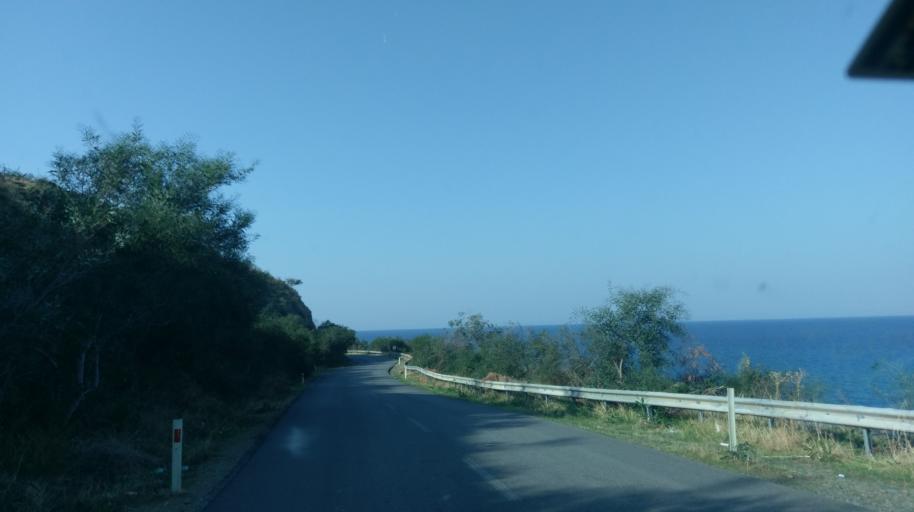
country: CY
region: Lefkosia
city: Lefka
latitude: 35.1524
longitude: 32.7928
